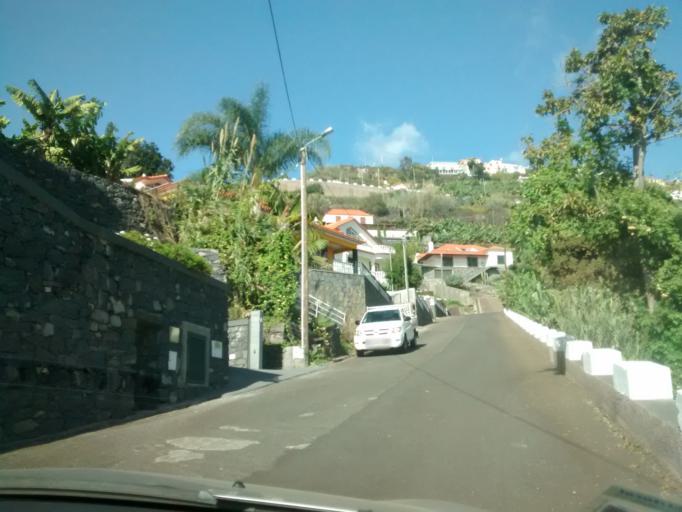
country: PT
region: Madeira
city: Calheta
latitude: 32.7187
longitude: -17.1701
